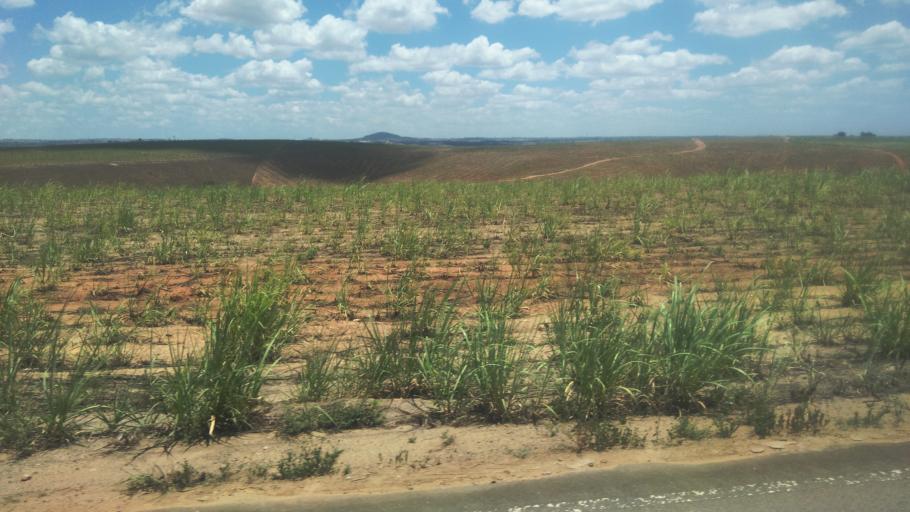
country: BR
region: Pernambuco
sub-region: Nazare Da Mata
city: Nazare da Mata
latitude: -7.7315
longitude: -35.2481
